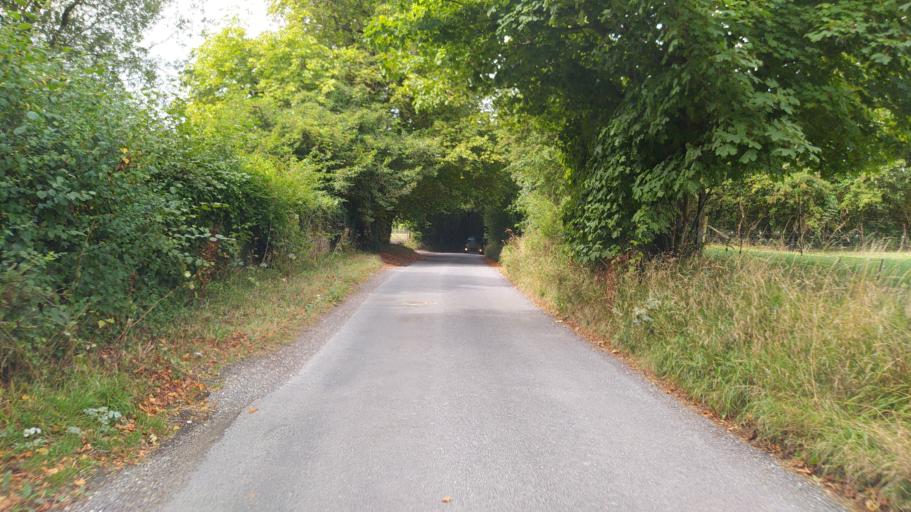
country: GB
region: England
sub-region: Hampshire
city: Petersfield
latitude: 50.9894
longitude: -1.0031
